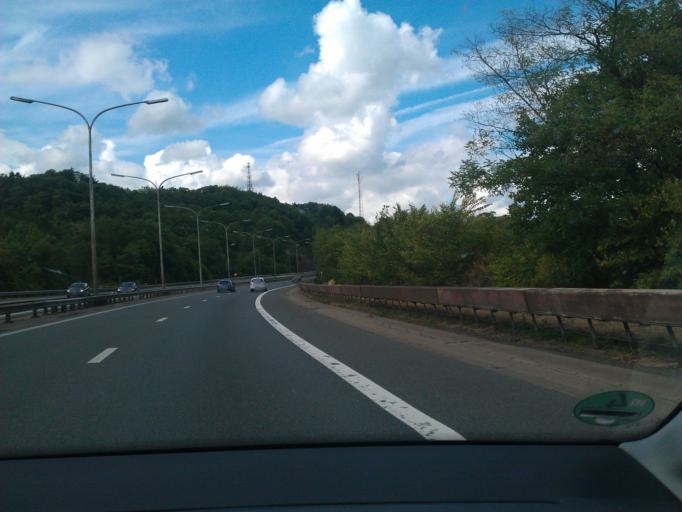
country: BE
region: Wallonia
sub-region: Province de Liege
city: Dison
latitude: 50.5936
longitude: 5.8439
